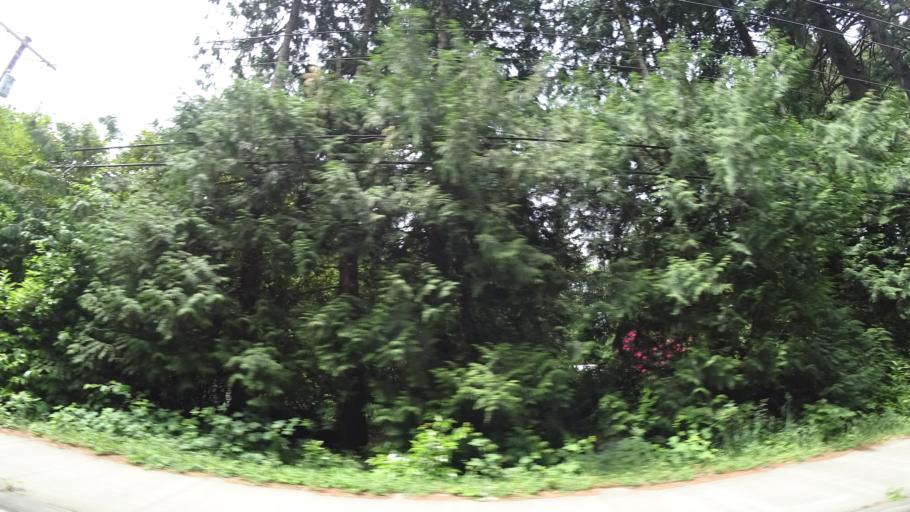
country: US
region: Oregon
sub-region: Washington County
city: Garden Home-Whitford
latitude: 45.4577
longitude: -122.7651
